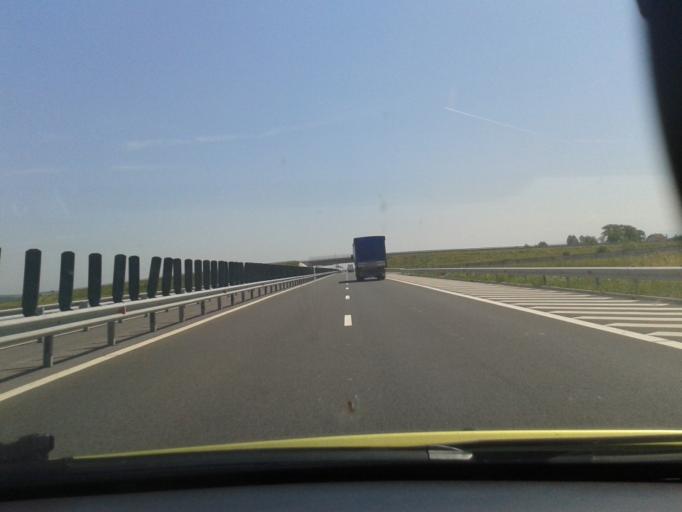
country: RO
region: Timis
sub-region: Comuna Balint
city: Balint
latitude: 45.7977
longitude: 21.8555
